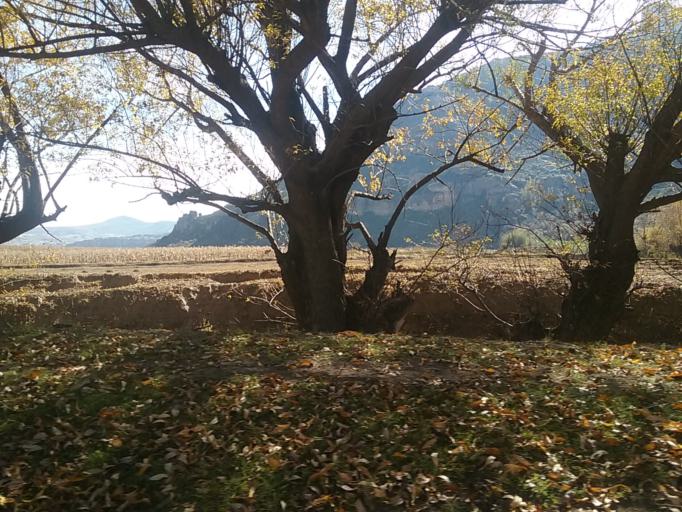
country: LS
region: Berea
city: Teyateyaneng
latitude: -29.2511
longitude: 27.9208
